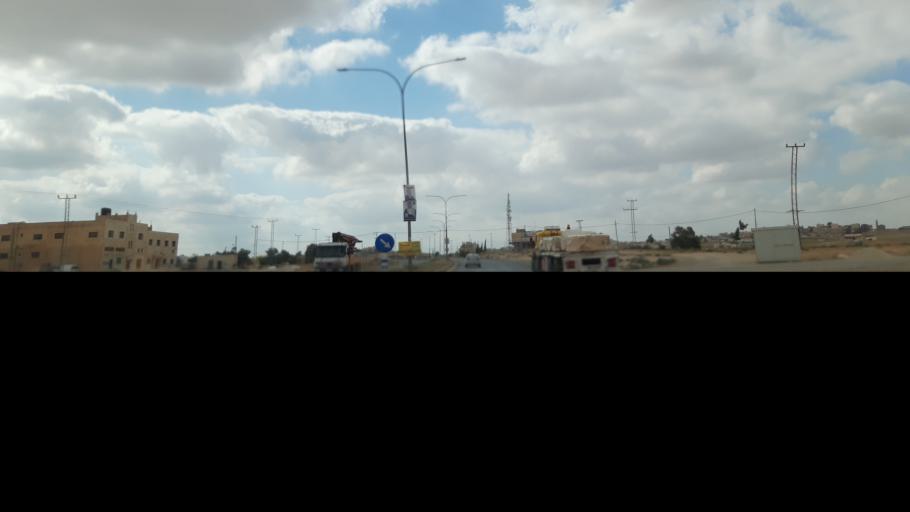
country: JO
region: Amman
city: Sahab
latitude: 31.8090
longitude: 36.1225
